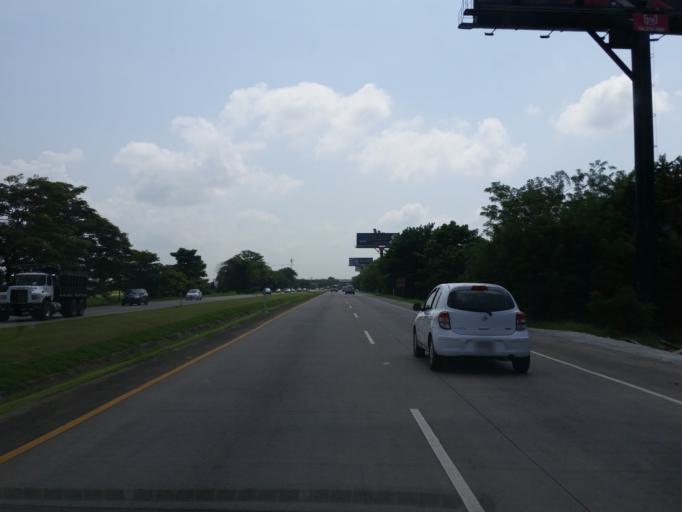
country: PA
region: Panama
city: San Miguelito
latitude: 9.0350
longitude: -79.4369
